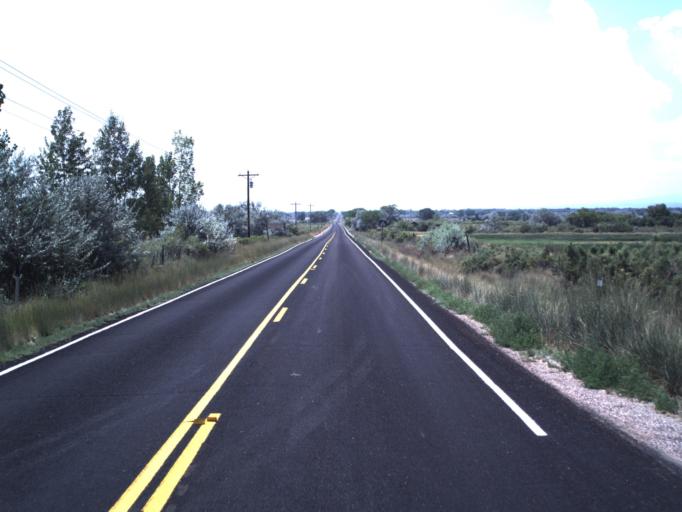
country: US
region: Utah
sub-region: Duchesne County
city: Roosevelt
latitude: 40.4037
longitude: -109.8408
